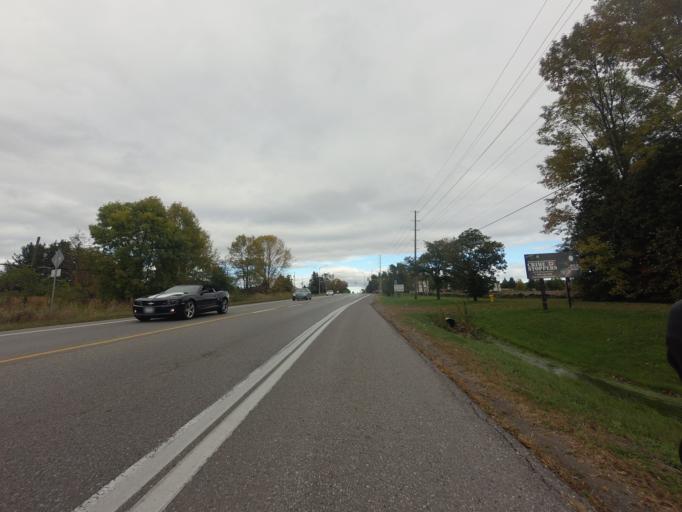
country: CA
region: Ontario
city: Cobourg
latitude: 43.9678
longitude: -78.2141
